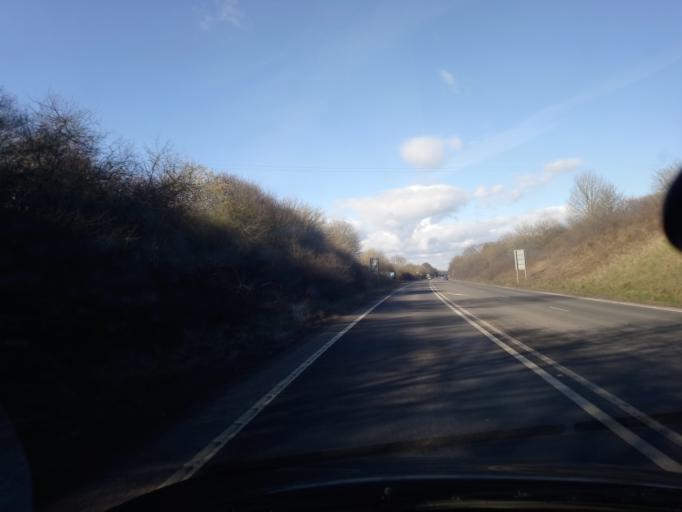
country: GB
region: England
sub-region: Shropshire
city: Whitchurch
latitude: 52.9586
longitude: -2.6959
